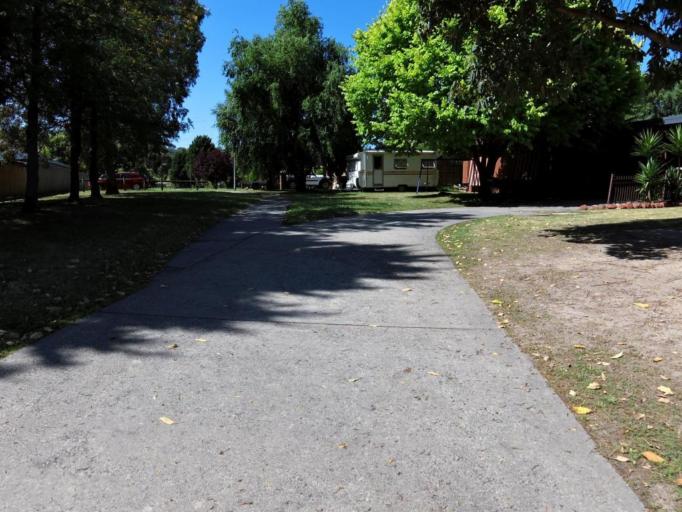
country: AU
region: Victoria
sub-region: Casey
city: Endeavour Hills
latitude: -37.9622
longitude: 145.2658
